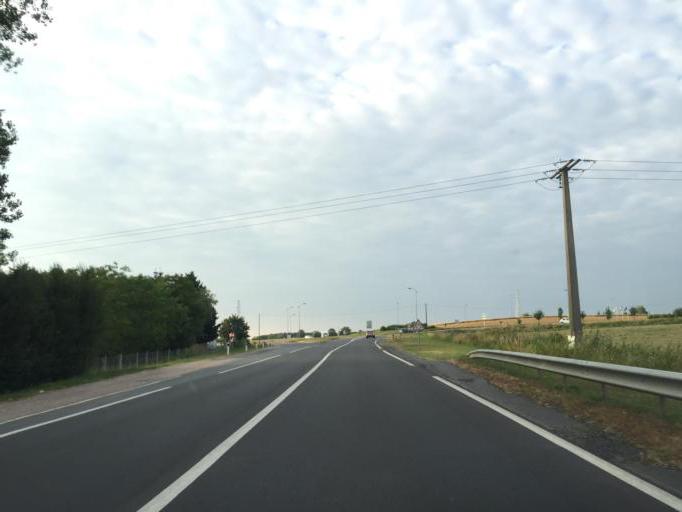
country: FR
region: Auvergne
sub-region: Departement de l'Allier
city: Varennes-sur-Allier
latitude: 46.3028
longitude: 3.4252
